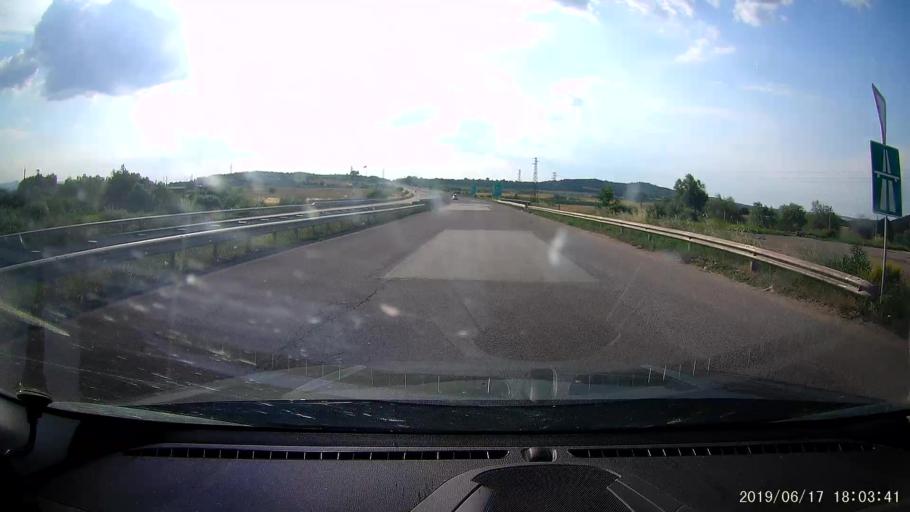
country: BG
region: Khaskovo
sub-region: Obshtina Svilengrad
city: Svilengrad
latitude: 41.7804
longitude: 26.2147
